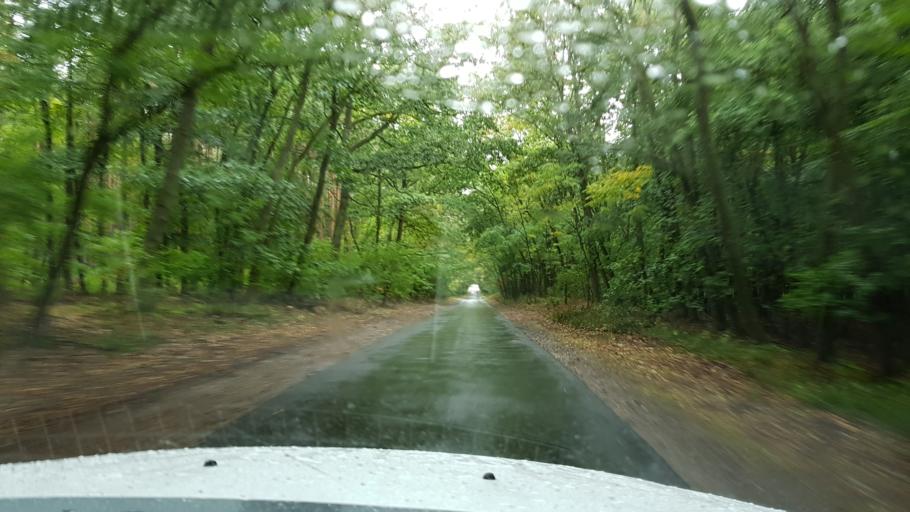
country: DE
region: Brandenburg
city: Meyenburg
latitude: 52.9765
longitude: 14.2260
